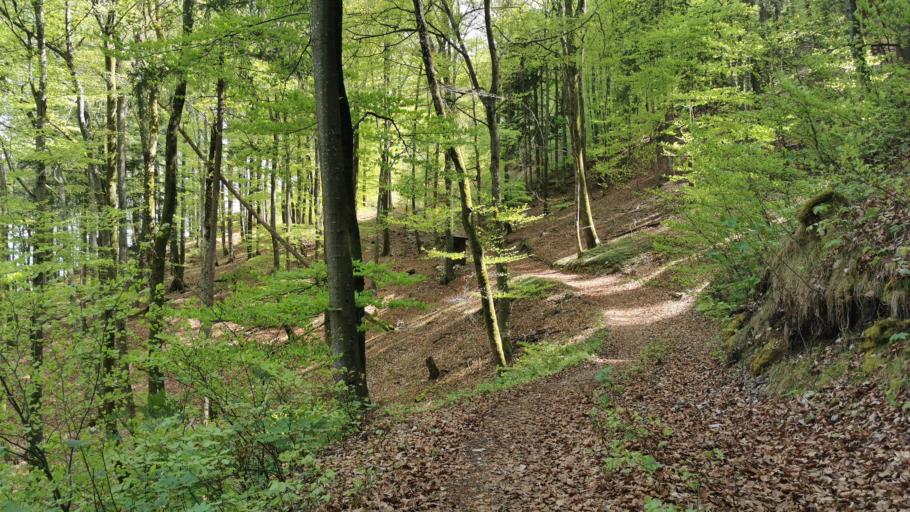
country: AT
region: Salzburg
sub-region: Politischer Bezirk Salzburg-Umgebung
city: Grodig
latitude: 47.7432
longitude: 13.0164
